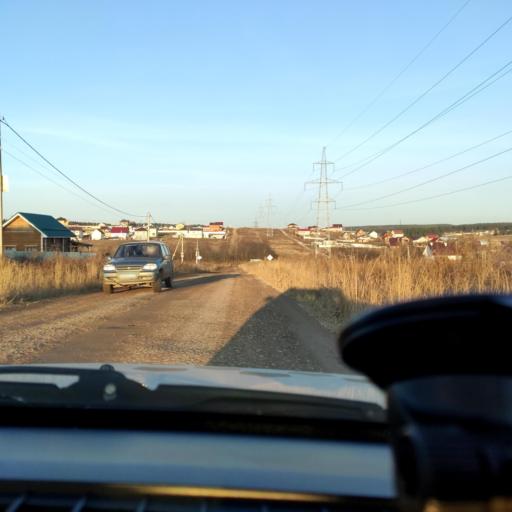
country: RU
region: Perm
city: Ferma
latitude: 57.9454
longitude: 56.3511
